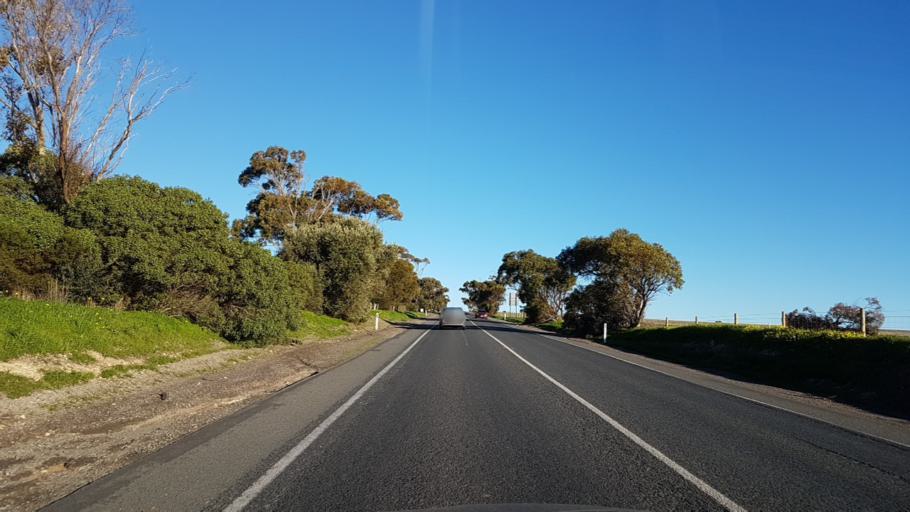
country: AU
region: South Australia
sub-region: Onkaparinga
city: Aldinga
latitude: -35.2449
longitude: 138.4943
